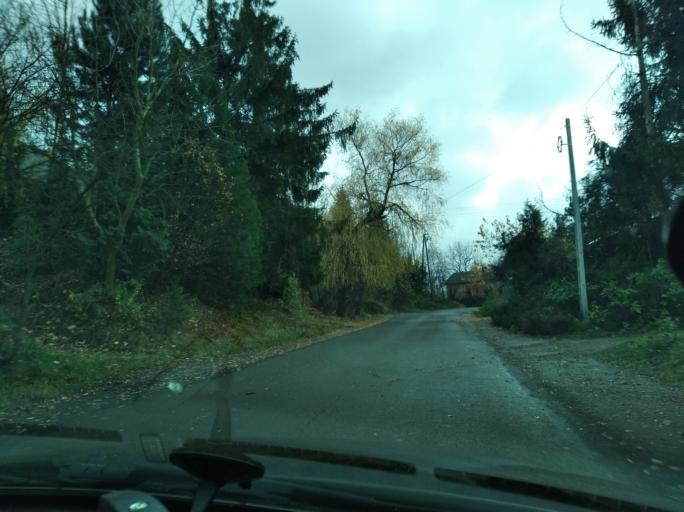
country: PL
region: Subcarpathian Voivodeship
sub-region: Powiat przeworski
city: Sietesz
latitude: 49.9755
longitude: 22.3408
